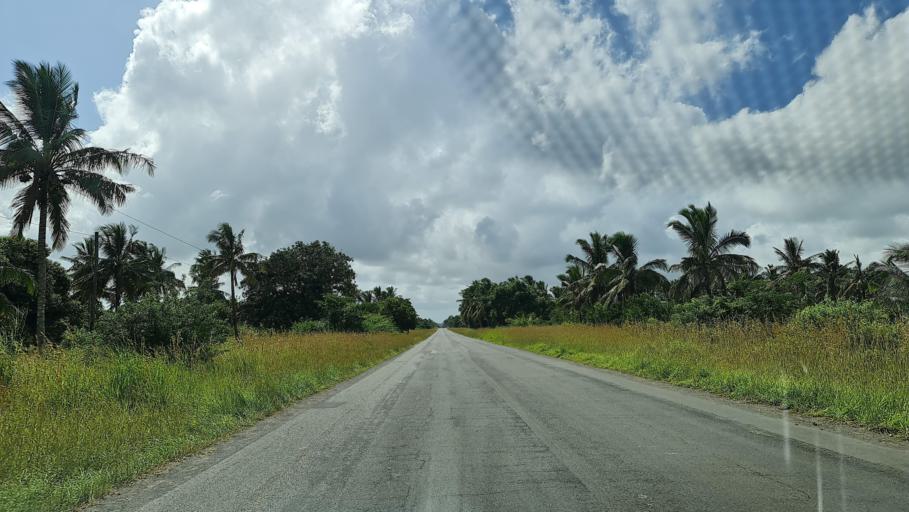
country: MZ
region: Gaza
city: Manjacaze
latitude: -24.6805
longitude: 34.6046
